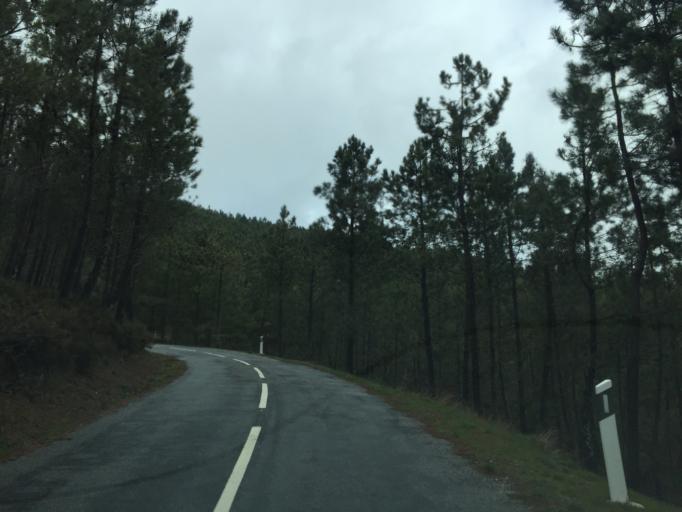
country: PT
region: Guarda
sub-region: Seia
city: Seia
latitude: 40.3363
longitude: -7.7160
